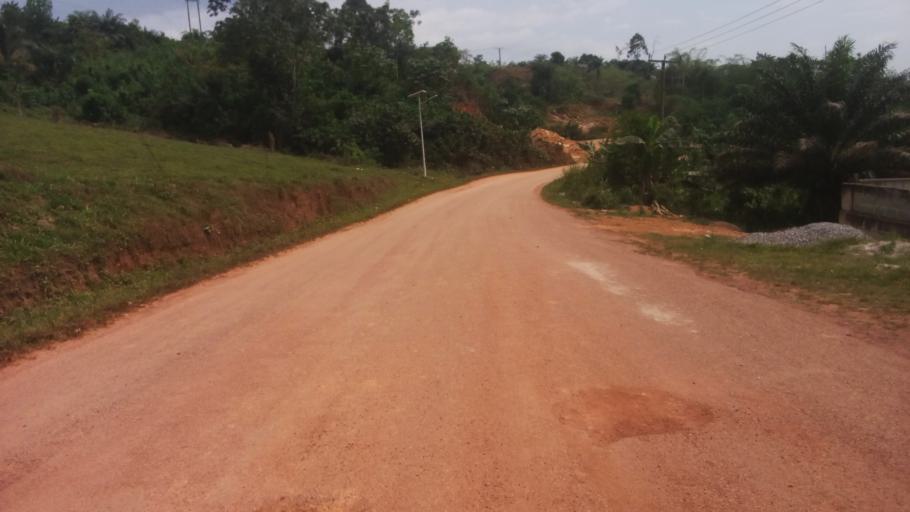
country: GH
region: Western
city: Tarkwa
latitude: 5.3037
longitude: -2.0021
